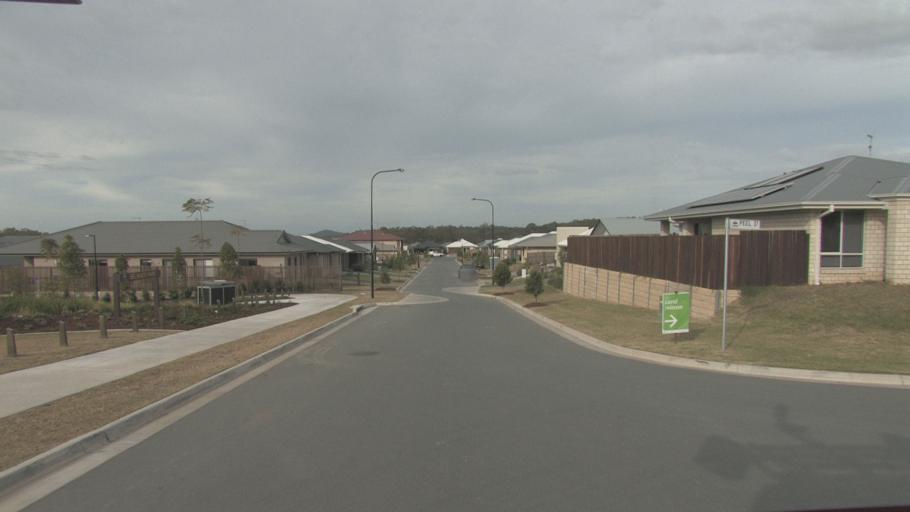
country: AU
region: Queensland
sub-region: Logan
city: Windaroo
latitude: -27.7201
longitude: 153.1619
